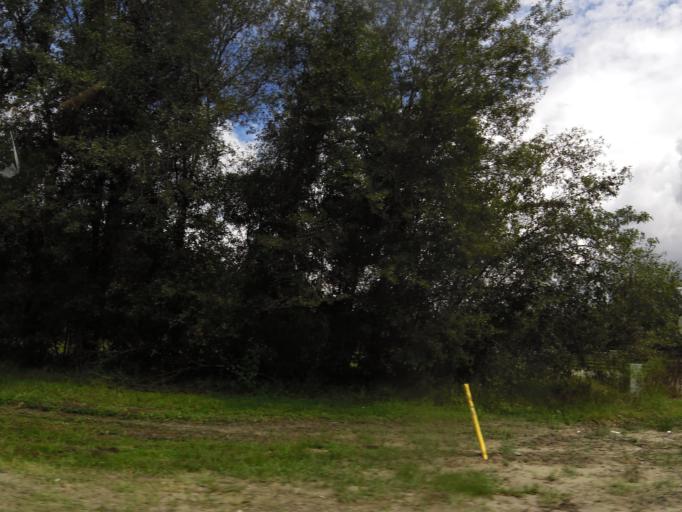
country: US
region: Florida
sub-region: Clay County
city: Middleburg
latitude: 30.1199
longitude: -81.9976
